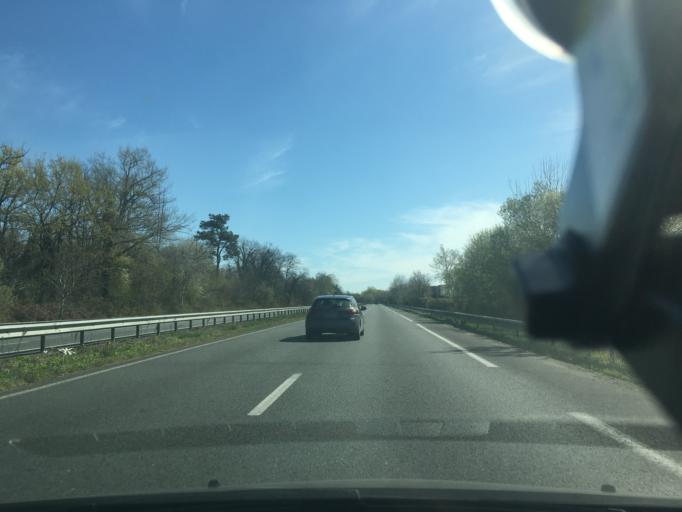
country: FR
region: Aquitaine
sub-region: Departement de la Gironde
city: Yvrac
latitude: 44.8685
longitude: -0.4587
